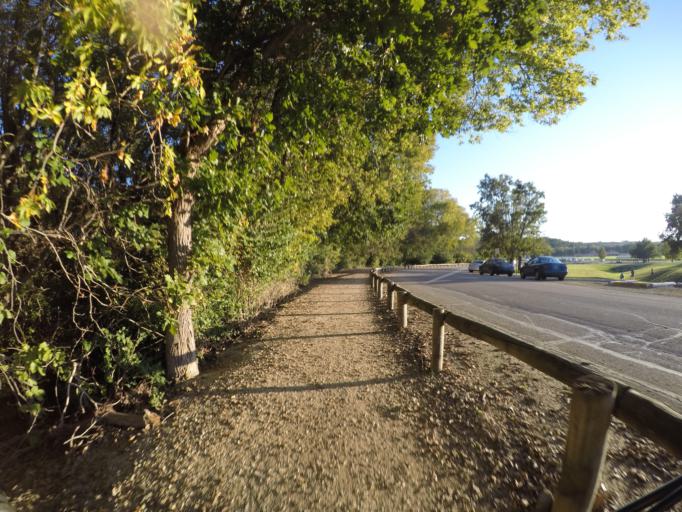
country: US
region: Kansas
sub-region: Riley County
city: Manhattan
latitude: 39.1861
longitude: -96.6294
